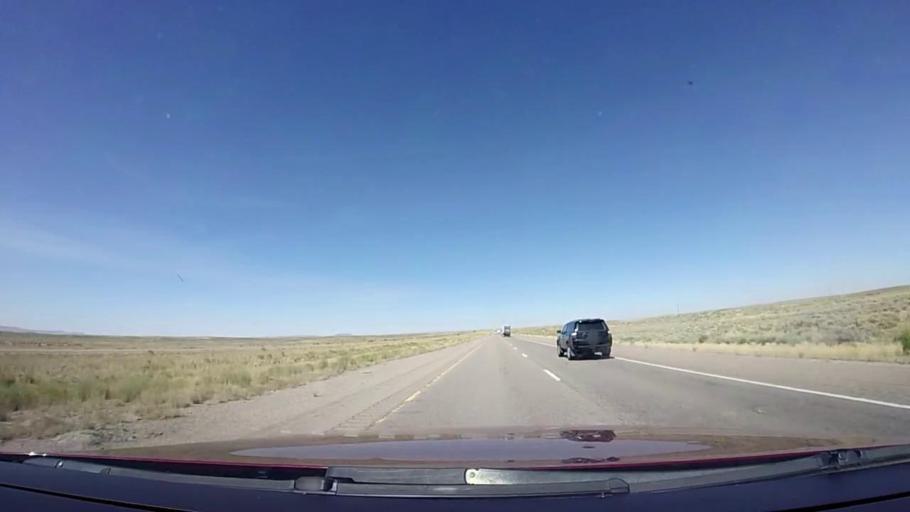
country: US
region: Wyoming
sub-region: Sweetwater County
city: Rock Springs
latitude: 41.6374
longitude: -108.4394
